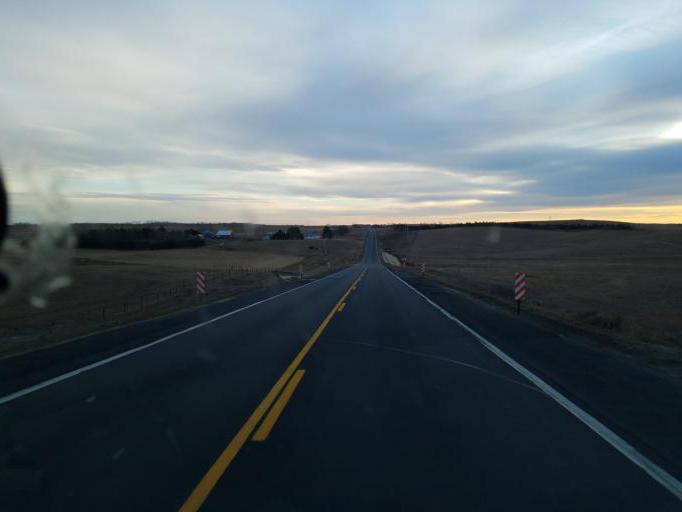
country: US
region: Nebraska
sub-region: Knox County
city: Center
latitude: 42.5971
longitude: -97.7752
